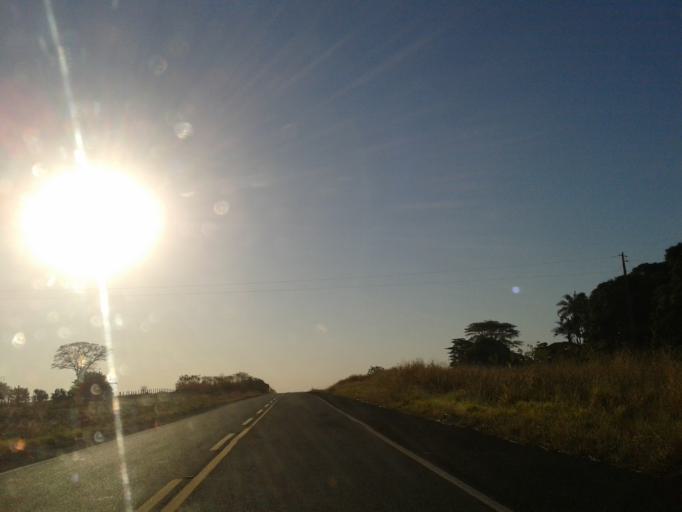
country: BR
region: Minas Gerais
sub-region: Santa Vitoria
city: Santa Vitoria
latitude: -19.0920
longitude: -50.3436
